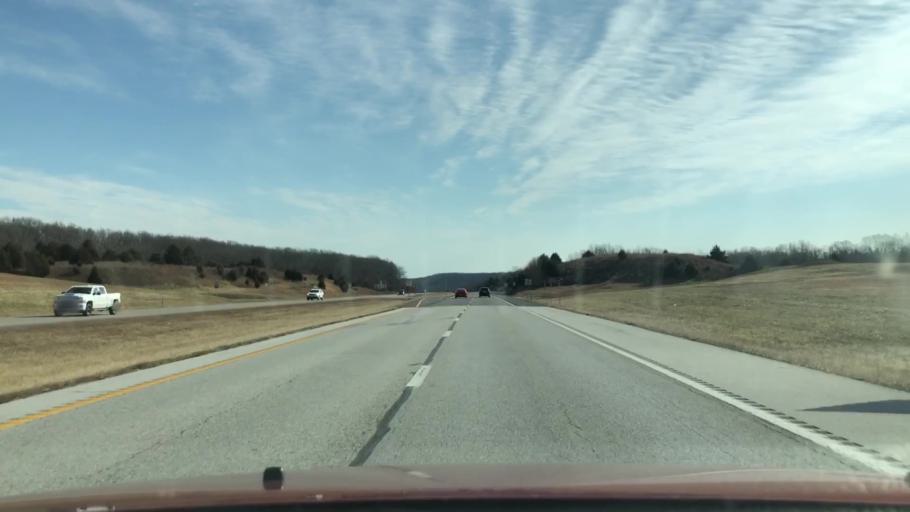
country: US
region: Missouri
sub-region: Wright County
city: Mansfield
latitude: 37.1158
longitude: -92.6765
